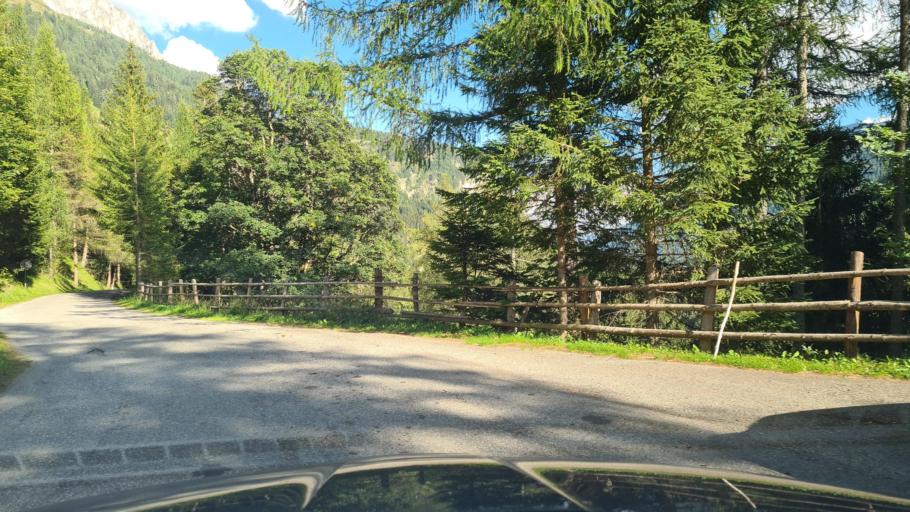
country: AT
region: Salzburg
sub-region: Politischer Bezirk Tamsweg
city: Zederhaus
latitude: 47.1844
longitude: 13.4329
